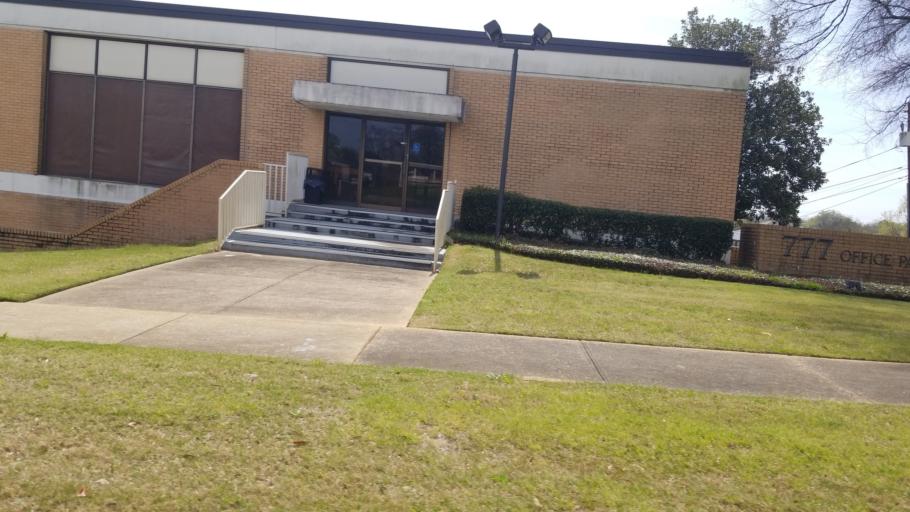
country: US
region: Alabama
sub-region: Montgomery County
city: Montgomery
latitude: 32.3673
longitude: -86.3056
